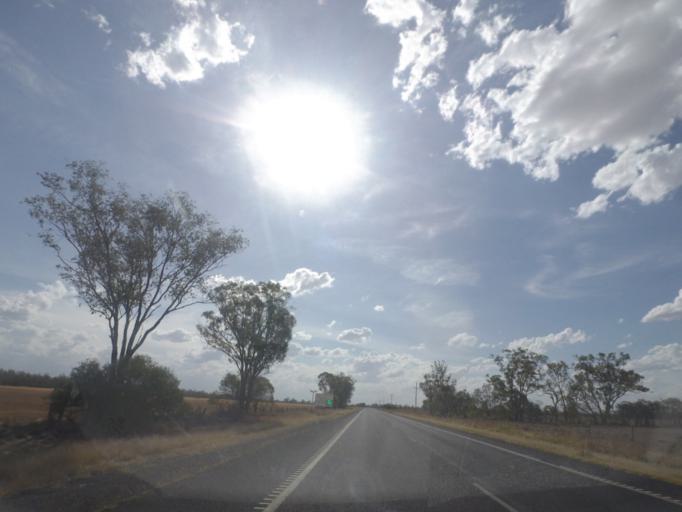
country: AU
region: New South Wales
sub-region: Moree Plains
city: Boggabilla
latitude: -28.5831
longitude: 150.8111
